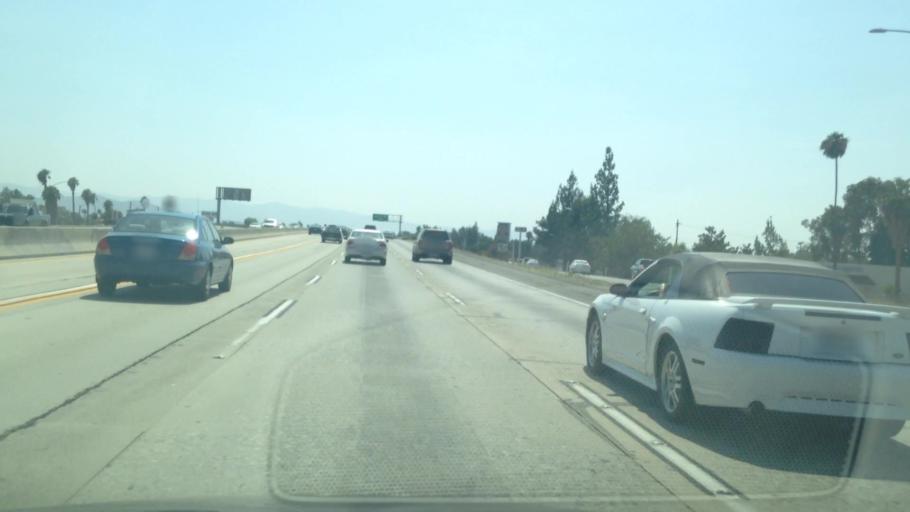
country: US
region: California
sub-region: Riverside County
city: Riverside
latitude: 33.9376
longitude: -117.4029
